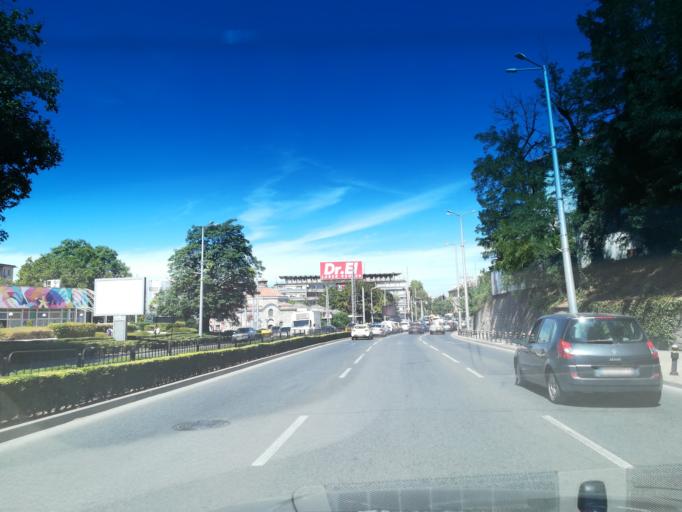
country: BG
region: Plovdiv
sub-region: Obshtina Plovdiv
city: Plovdiv
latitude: 42.1506
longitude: 24.7504
